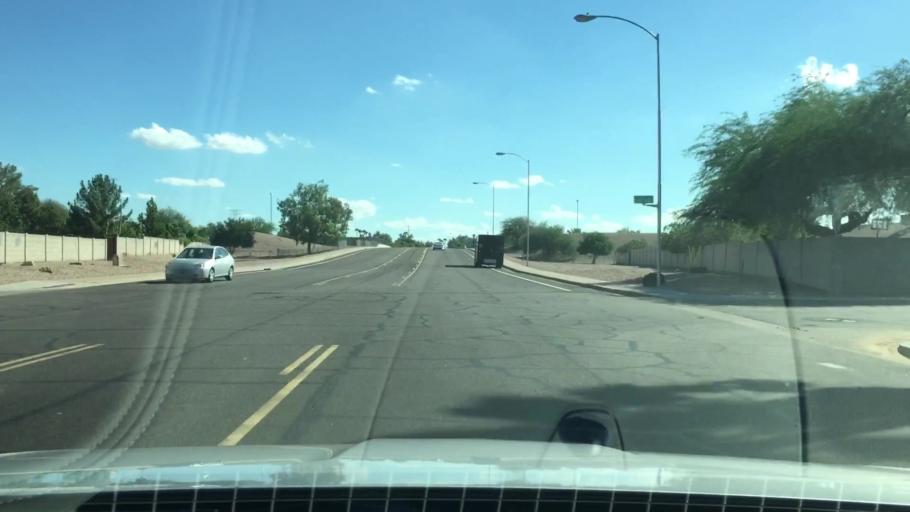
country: US
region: Arizona
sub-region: Maricopa County
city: Gilbert
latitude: 33.3887
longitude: -111.7473
